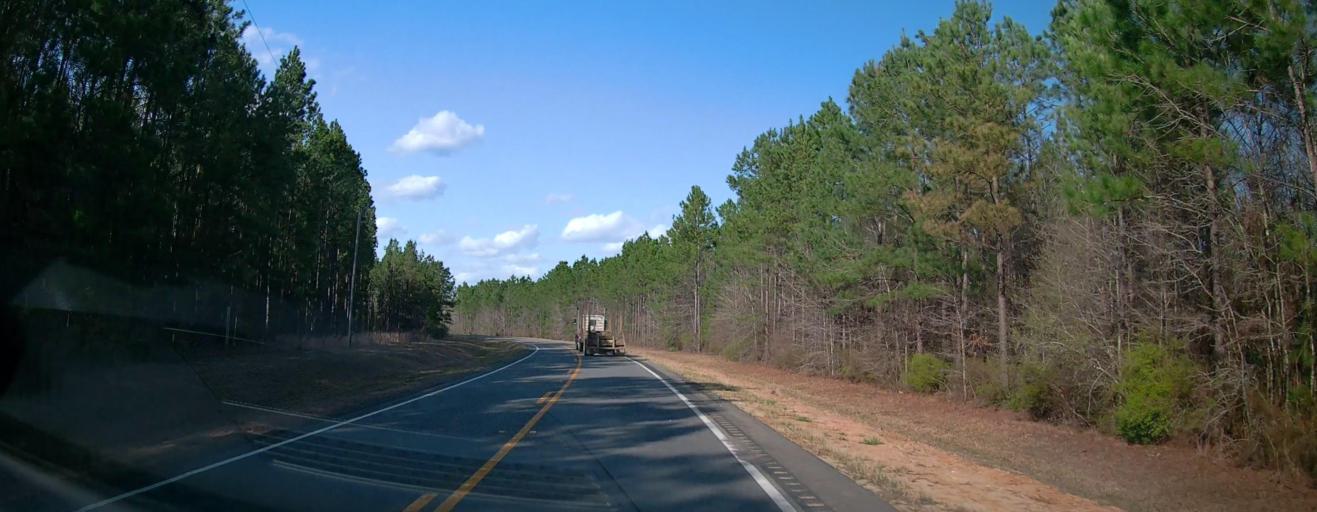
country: US
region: Georgia
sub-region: Telfair County
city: McRae
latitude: 32.0585
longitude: -82.8125
